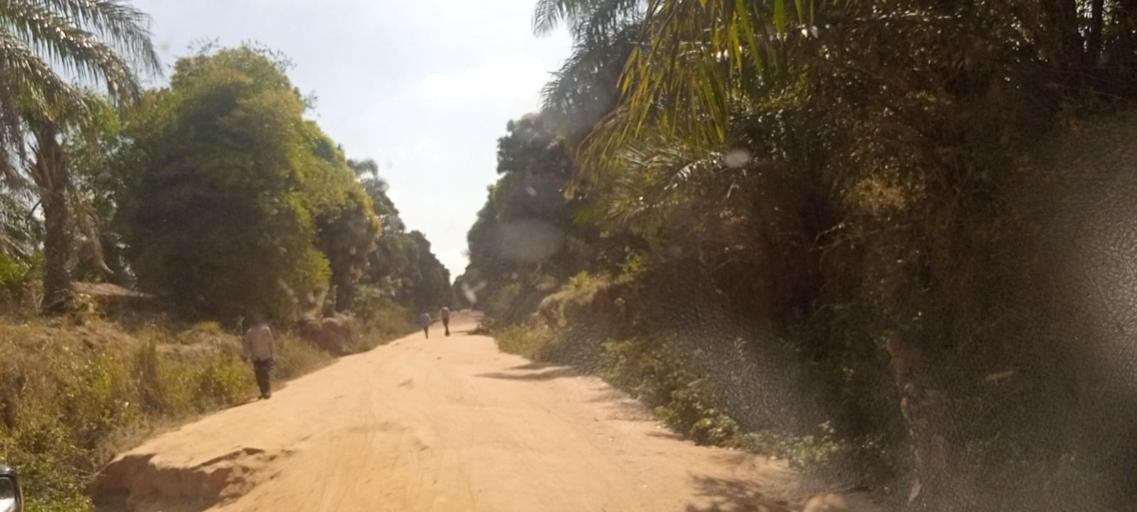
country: CD
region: Kasai-Oriental
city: Kabinda
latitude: -6.1297
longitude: 24.5050
